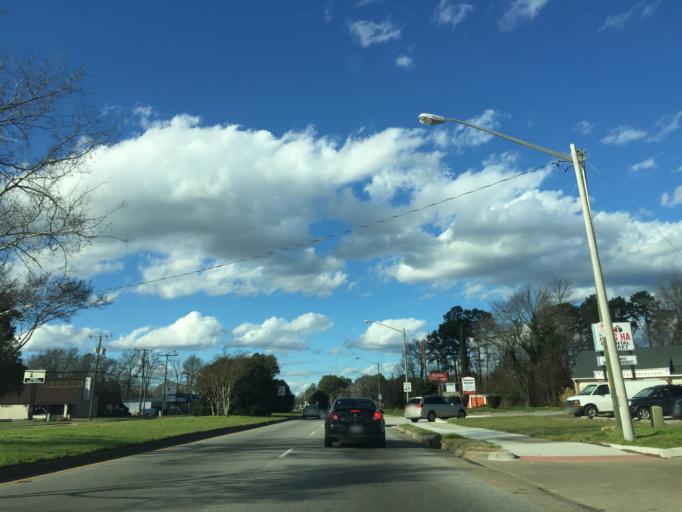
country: US
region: Virginia
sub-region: York County
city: Yorktown
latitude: 37.1142
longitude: -76.5193
